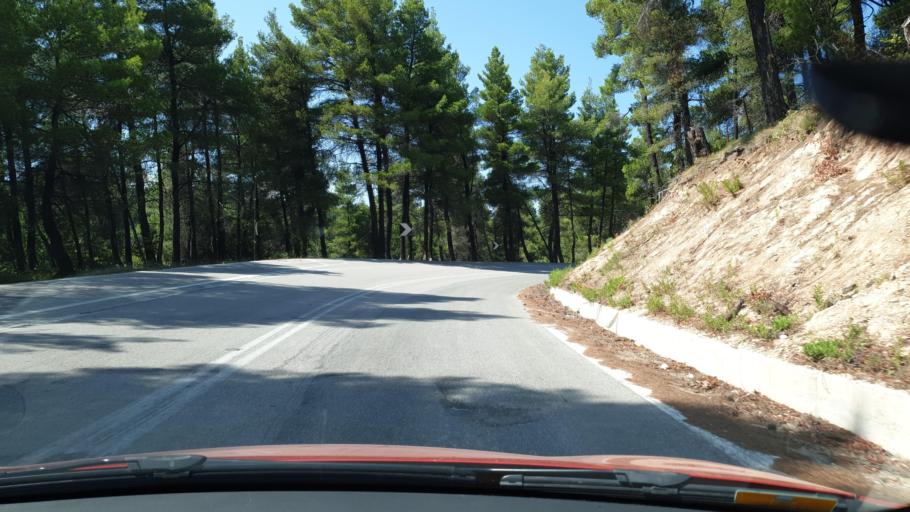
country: GR
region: Central Greece
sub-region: Nomos Evvoias
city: Politika
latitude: 38.6517
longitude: 23.5630
